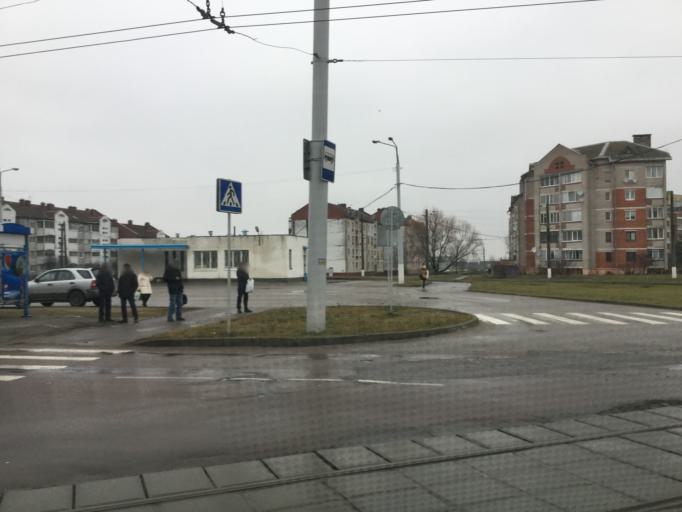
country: BY
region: Vitebsk
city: Vitebsk
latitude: 55.1973
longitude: 30.2656
